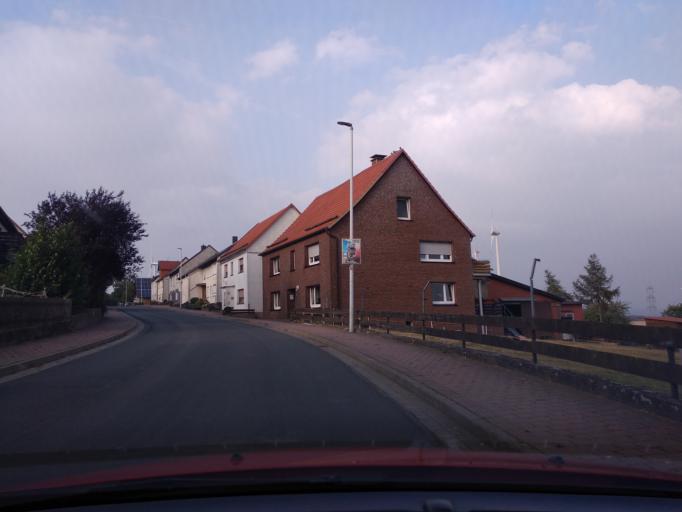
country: DE
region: North Rhine-Westphalia
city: Beverungen
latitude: 51.6227
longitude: 9.3412
